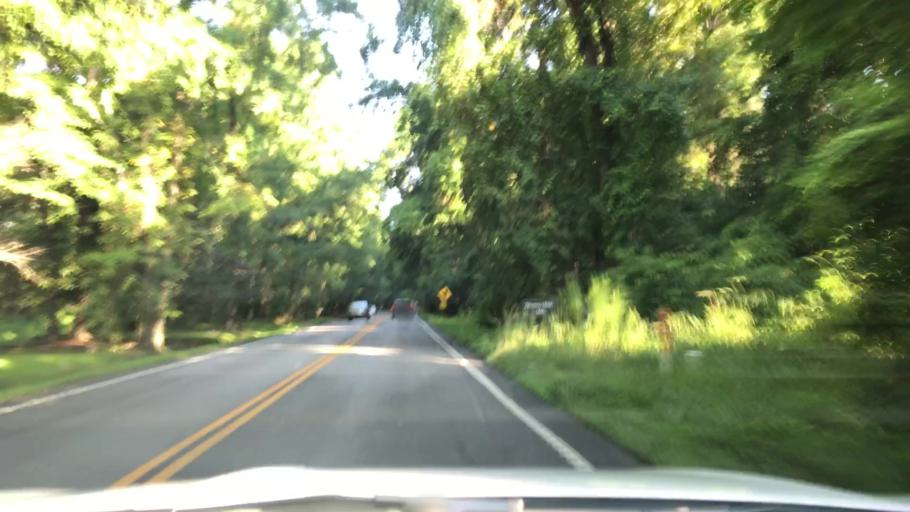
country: US
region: South Carolina
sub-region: Charleston County
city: Shell Point
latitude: 32.8581
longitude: -80.0752
